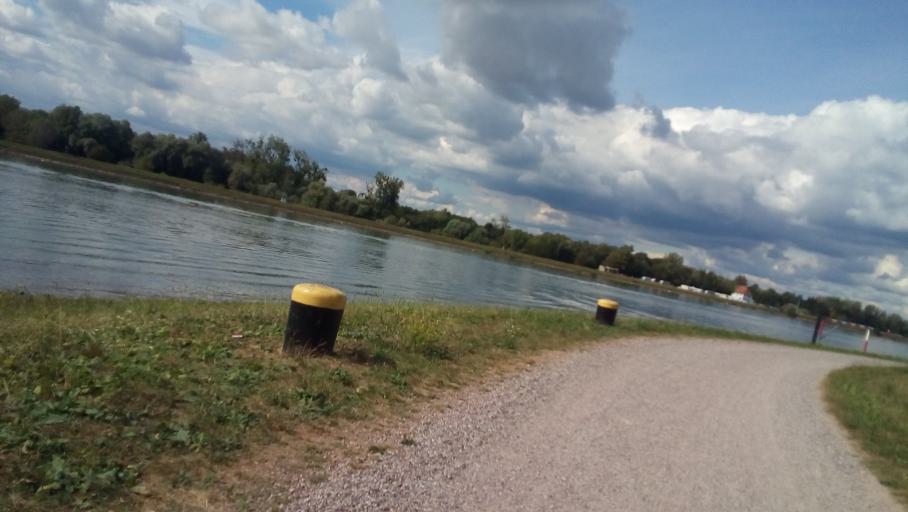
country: FR
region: Alsace
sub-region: Departement du Bas-Rhin
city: Drusenheim
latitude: 48.7498
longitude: 7.9701
